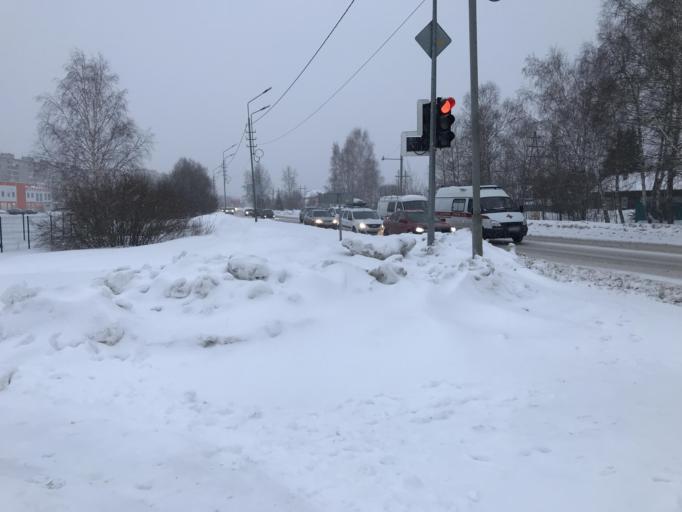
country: RU
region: Tjumen
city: Tobol'sk
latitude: 58.2339
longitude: 68.2638
